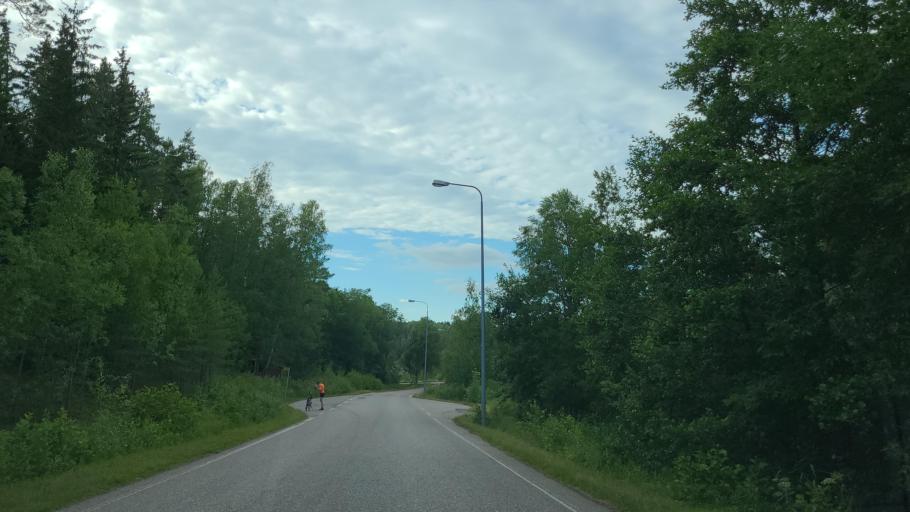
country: FI
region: Varsinais-Suomi
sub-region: Turku
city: Rymaettylae
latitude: 60.3390
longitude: 21.9788
